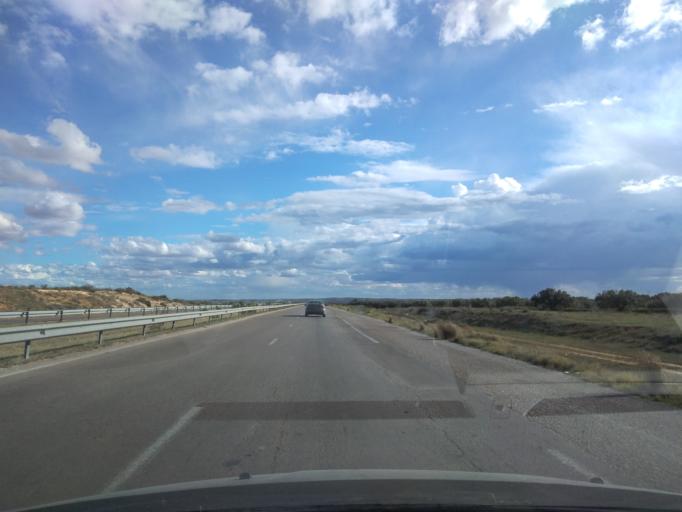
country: TN
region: Al Munastir
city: Manzil Kamil
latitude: 35.6112
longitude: 10.5971
